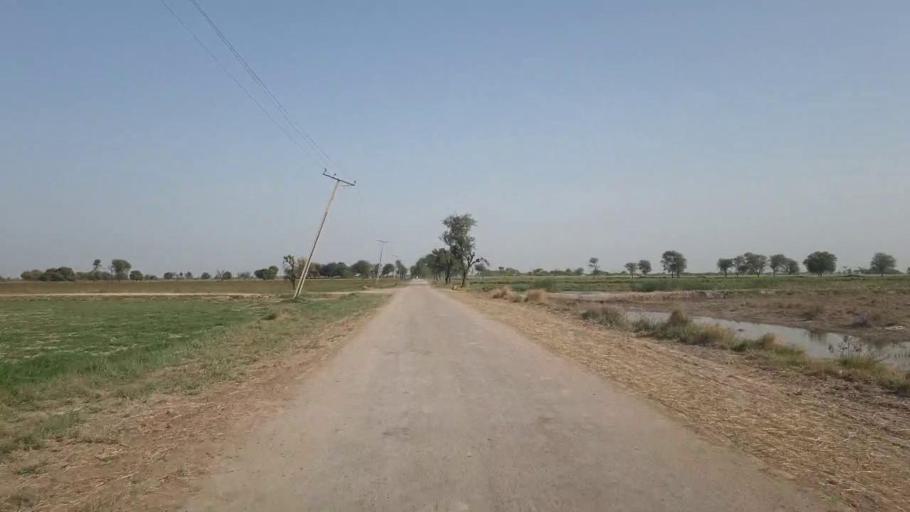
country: PK
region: Sindh
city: Dhoro Naro
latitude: 25.4619
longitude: 69.5598
